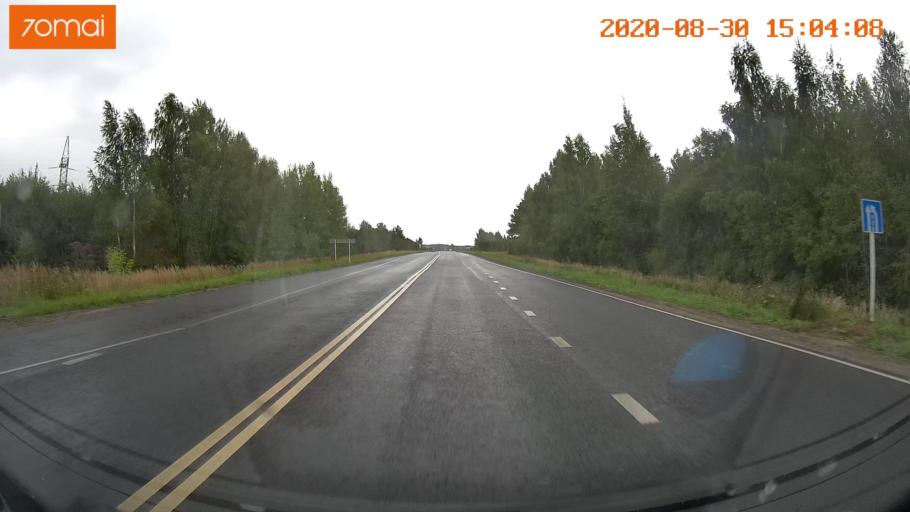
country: RU
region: Ivanovo
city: Staraya Vichuga
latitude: 57.2908
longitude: 41.9073
